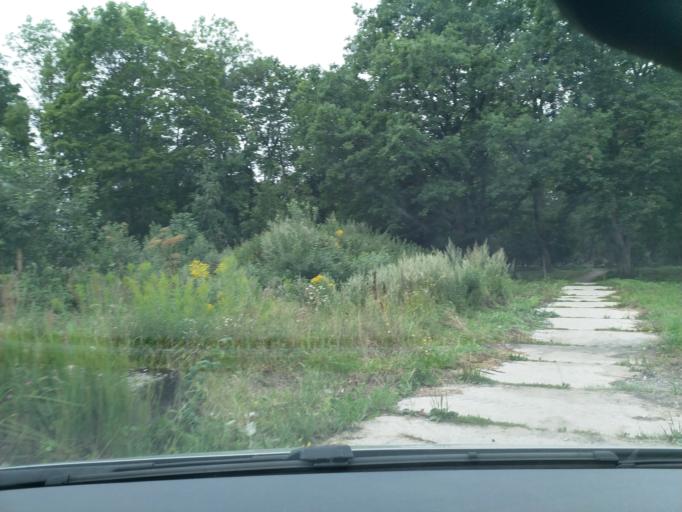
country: LV
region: Kuldigas Rajons
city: Kuldiga
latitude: 56.9658
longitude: 21.9787
